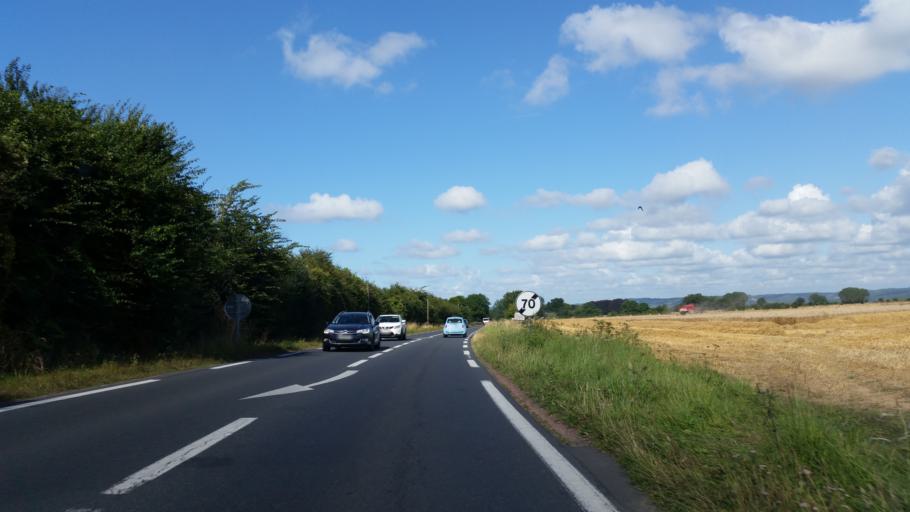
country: FR
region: Lower Normandy
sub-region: Departement du Calvados
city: Bavent
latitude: 49.2455
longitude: -0.1825
